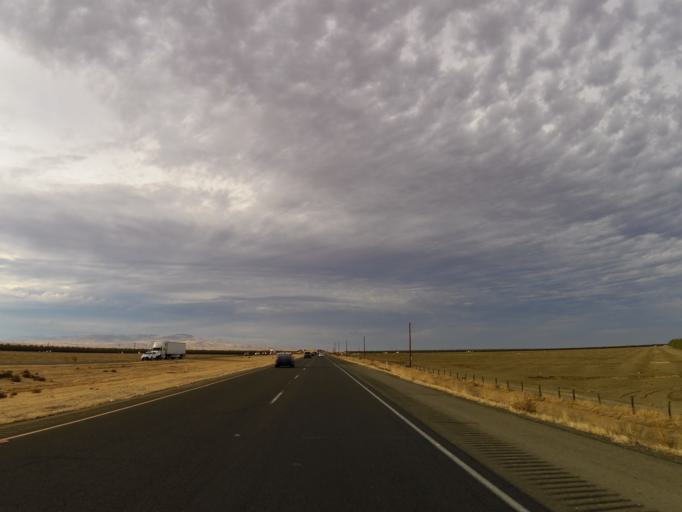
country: US
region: California
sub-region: Fresno County
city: Huron
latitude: 36.1687
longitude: -120.1870
